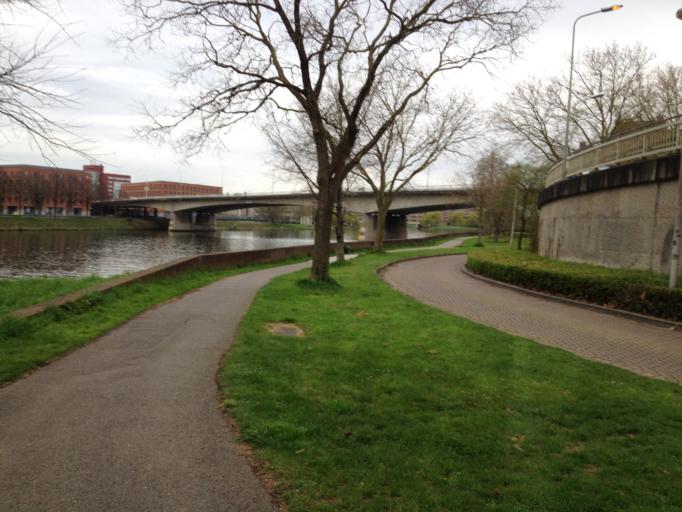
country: NL
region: Limburg
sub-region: Gemeente Maastricht
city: Maastricht
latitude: 50.8433
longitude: 5.6978
